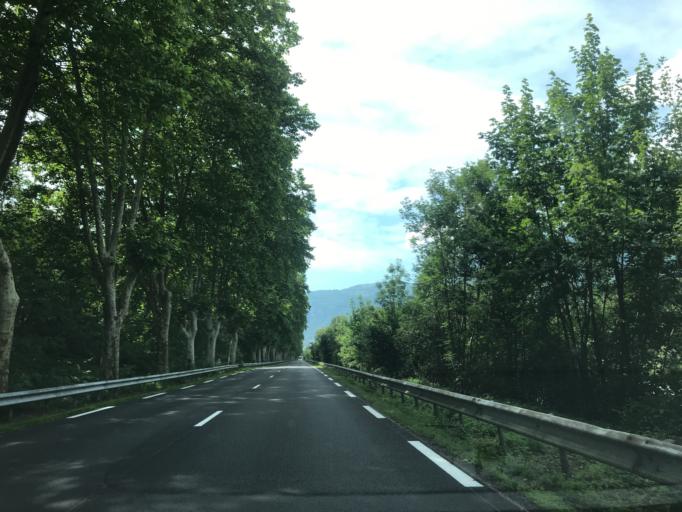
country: FR
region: Rhone-Alpes
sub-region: Departement de la Savoie
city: Aiton
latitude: 45.5584
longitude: 6.2261
